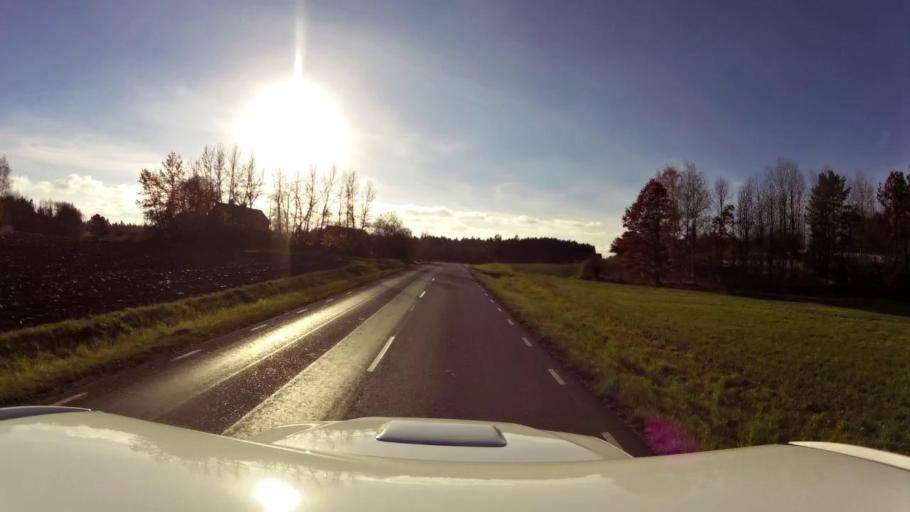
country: SE
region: OEstergoetland
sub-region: Linkopings Kommun
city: Vikingstad
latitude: 58.3023
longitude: 15.4780
